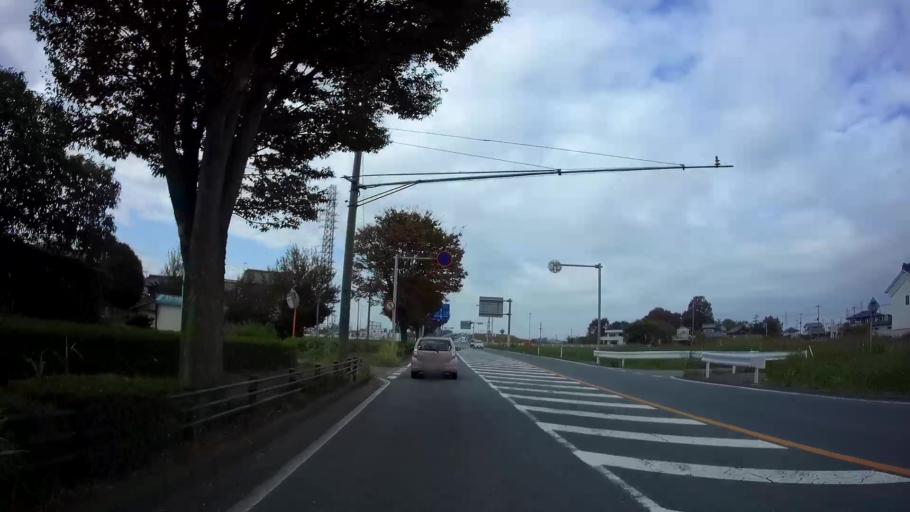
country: JP
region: Saitama
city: Fukayacho
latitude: 36.2101
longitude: 139.3020
